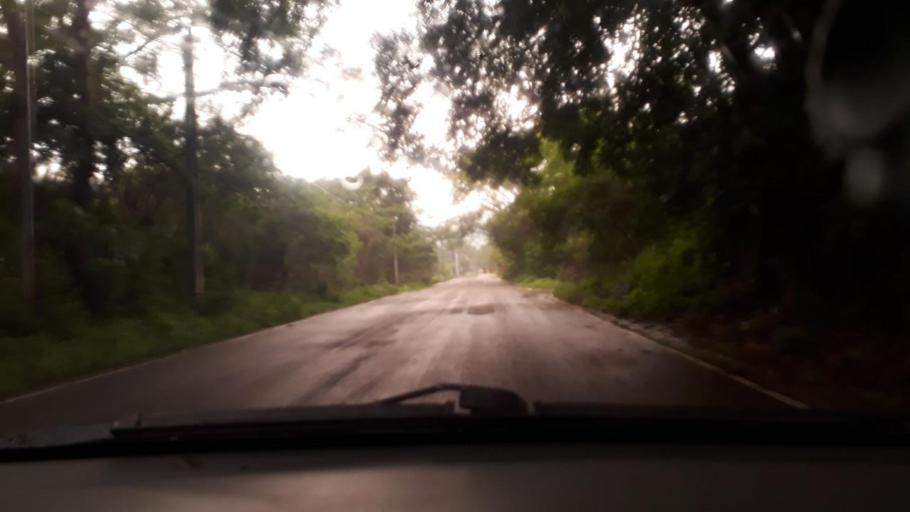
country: GT
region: Jutiapa
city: Comapa
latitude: 14.0524
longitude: -89.9334
